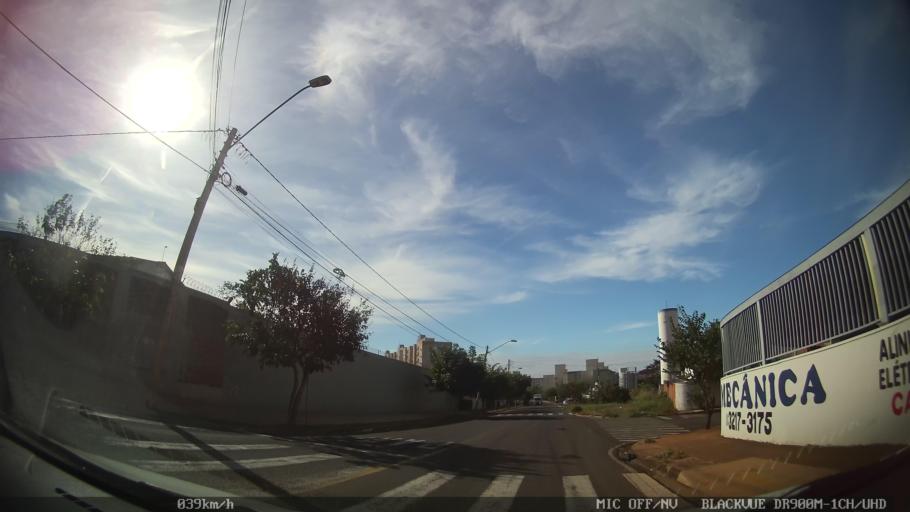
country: BR
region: Sao Paulo
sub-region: Sao Jose Do Rio Preto
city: Sao Jose do Rio Preto
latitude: -20.7890
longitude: -49.3507
